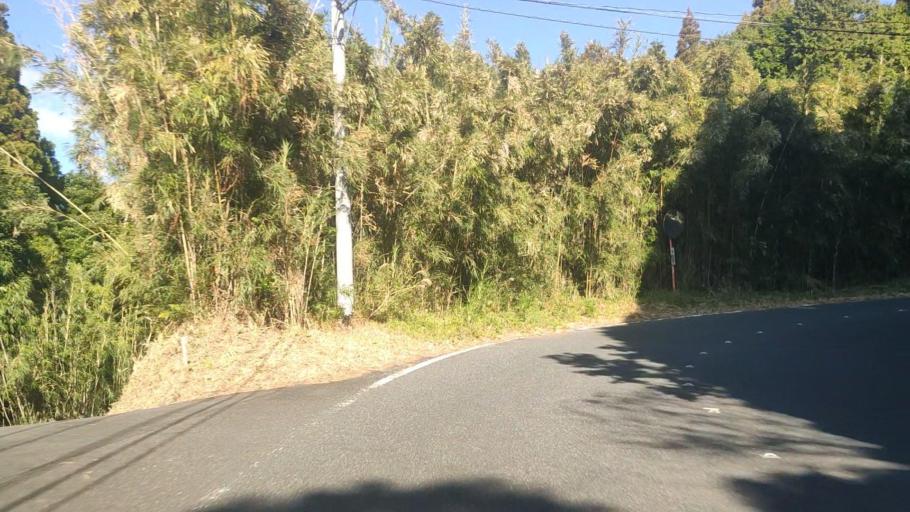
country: JP
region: Kagoshima
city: Kokubu-matsuki
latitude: 31.6717
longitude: 130.8297
